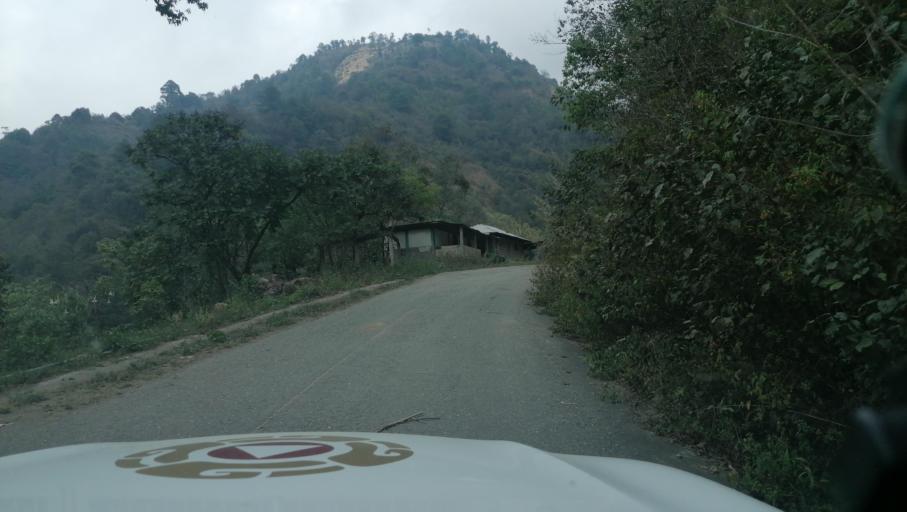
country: GT
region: San Marcos
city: Tacana
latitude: 15.2205
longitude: -92.2013
